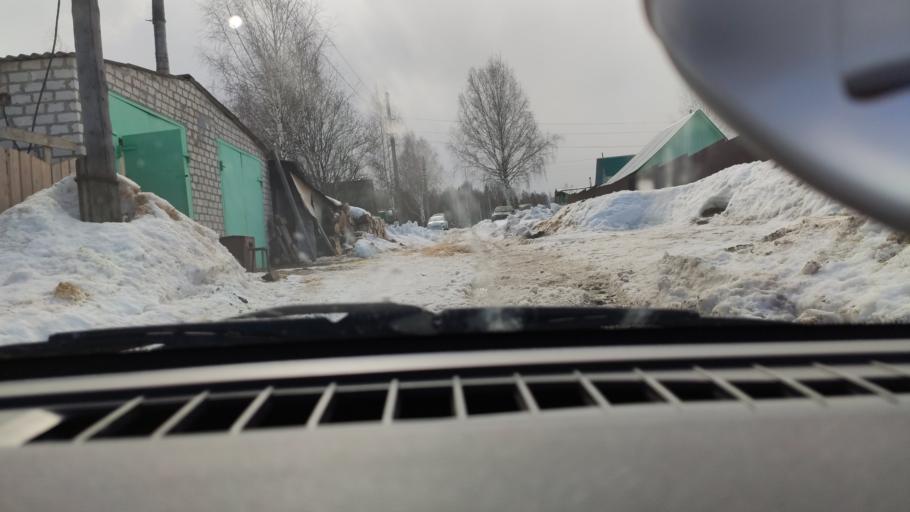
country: RU
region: Perm
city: Nytva
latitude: 57.9239
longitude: 55.4344
